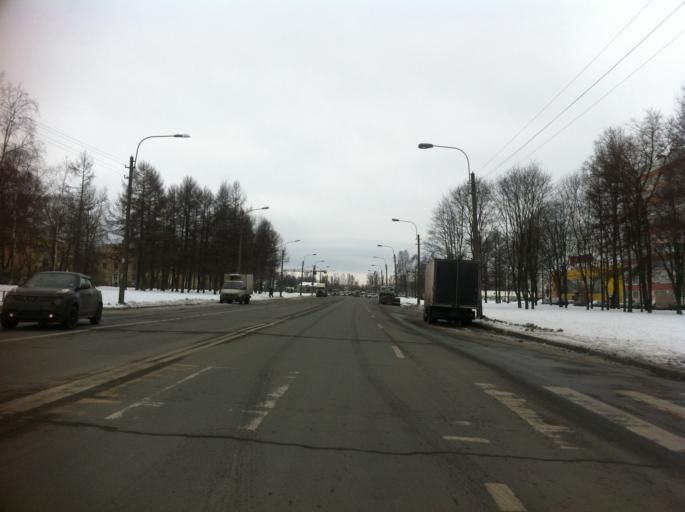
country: RU
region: St.-Petersburg
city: Uritsk
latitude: 59.8273
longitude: 30.1757
